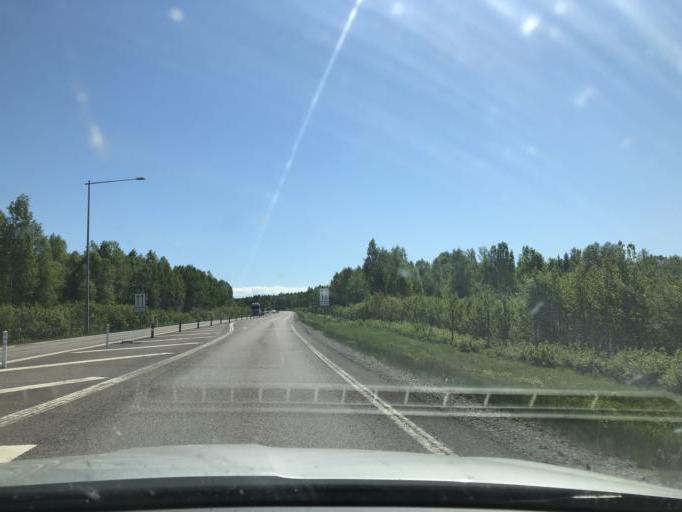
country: SE
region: Norrbotten
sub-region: Kalix Kommun
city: Rolfs
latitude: 65.8875
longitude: 22.9201
